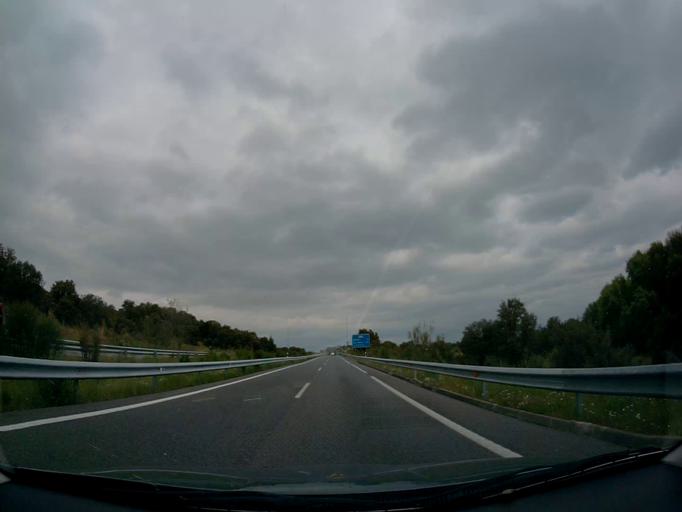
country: ES
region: Madrid
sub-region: Provincia de Madrid
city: Villaviciosa de Odon
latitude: 40.3707
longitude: -3.9494
